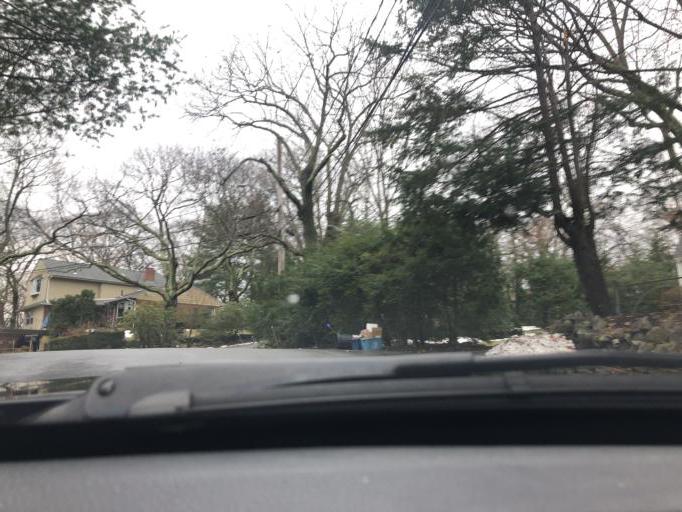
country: US
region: Massachusetts
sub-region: Middlesex County
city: Arlington
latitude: 42.4255
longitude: -71.1585
